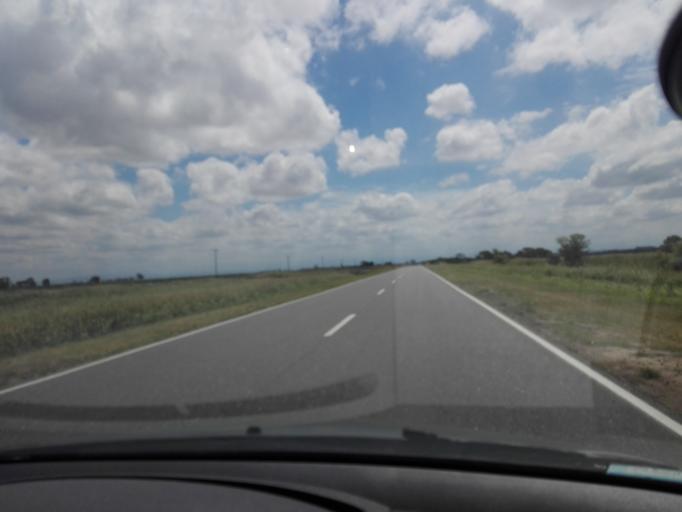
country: AR
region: Cordoba
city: Toledo
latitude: -31.6462
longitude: -64.0427
